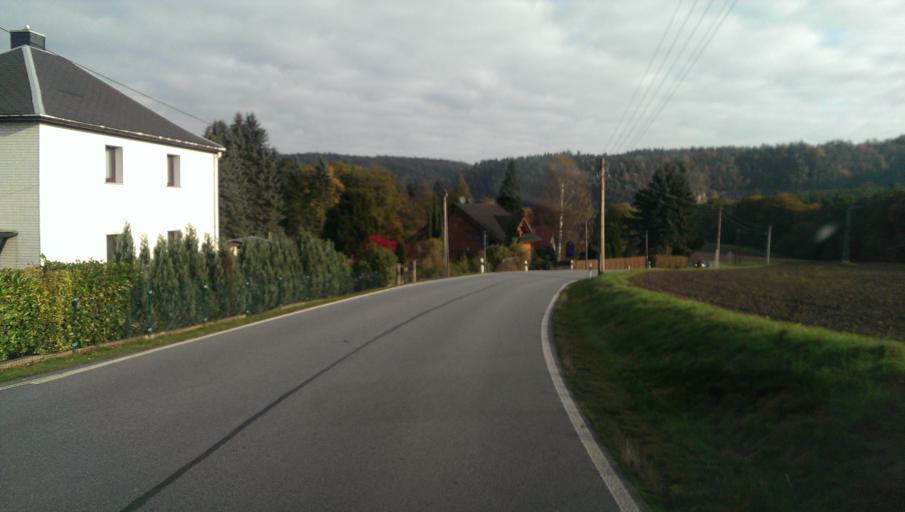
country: DE
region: Saxony
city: Porschdorf
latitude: 50.9523
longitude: 14.1070
